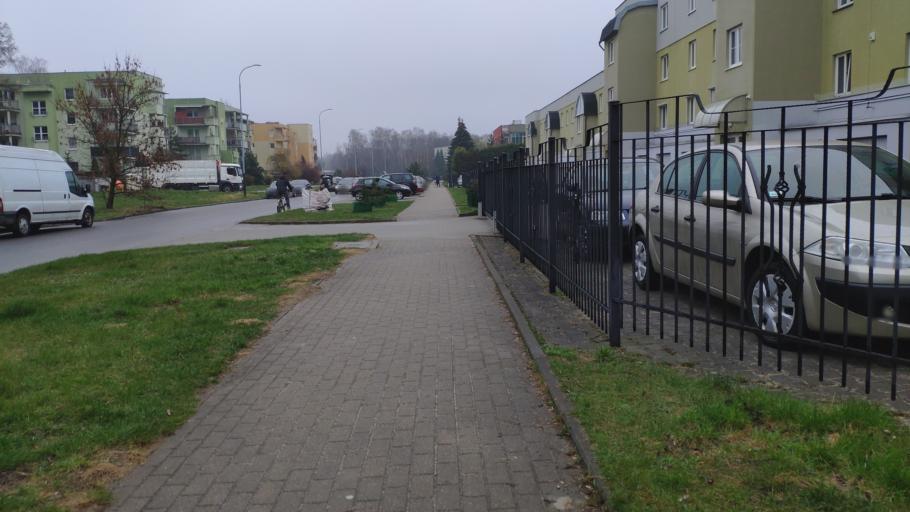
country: PL
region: Lodz Voivodeship
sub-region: Powiat lodzki wschodni
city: Andrespol
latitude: 51.7528
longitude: 19.5665
